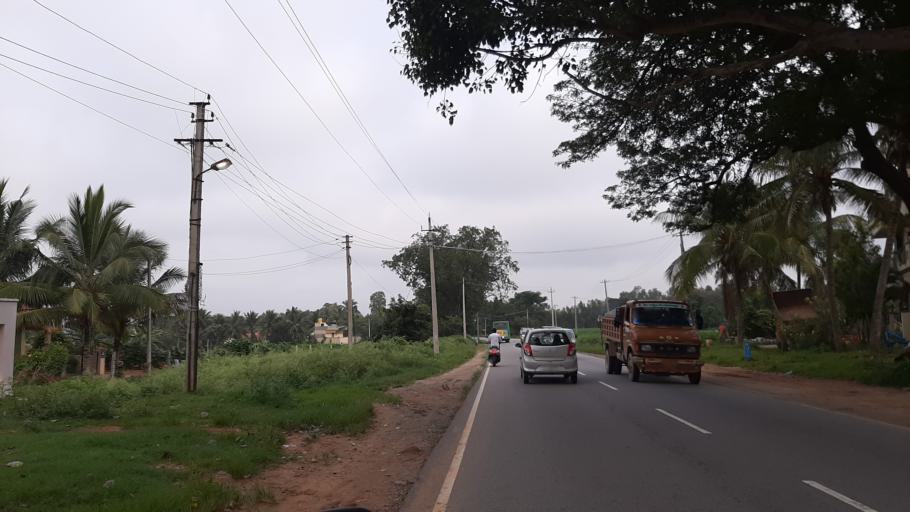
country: IN
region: Karnataka
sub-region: Bangalore Rural
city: Nelamangala
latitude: 12.9680
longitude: 77.3784
